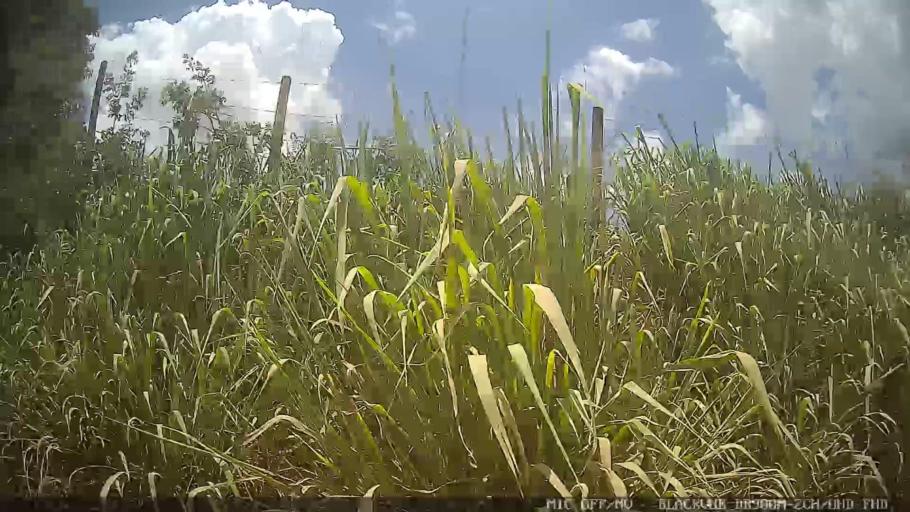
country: BR
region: Sao Paulo
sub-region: Atibaia
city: Atibaia
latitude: -23.1104
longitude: -46.6200
